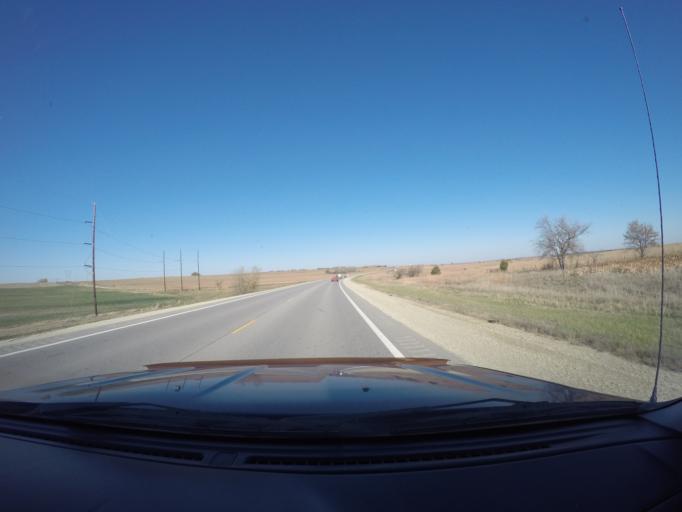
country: US
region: Kansas
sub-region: Riley County
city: Ogden
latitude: 39.2906
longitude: -96.7520
